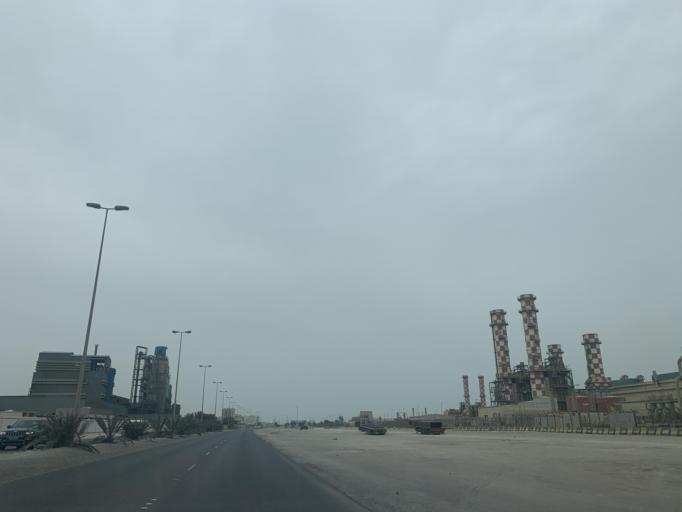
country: BH
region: Muharraq
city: Al Hadd
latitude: 26.2159
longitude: 50.6579
